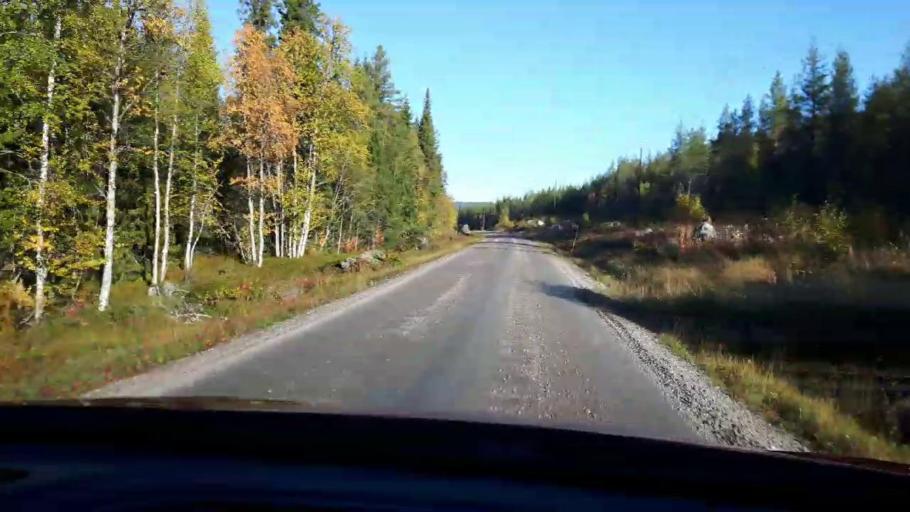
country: SE
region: Jaemtland
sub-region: Stroemsunds Kommun
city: Stroemsund
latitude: 64.3661
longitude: 15.1649
